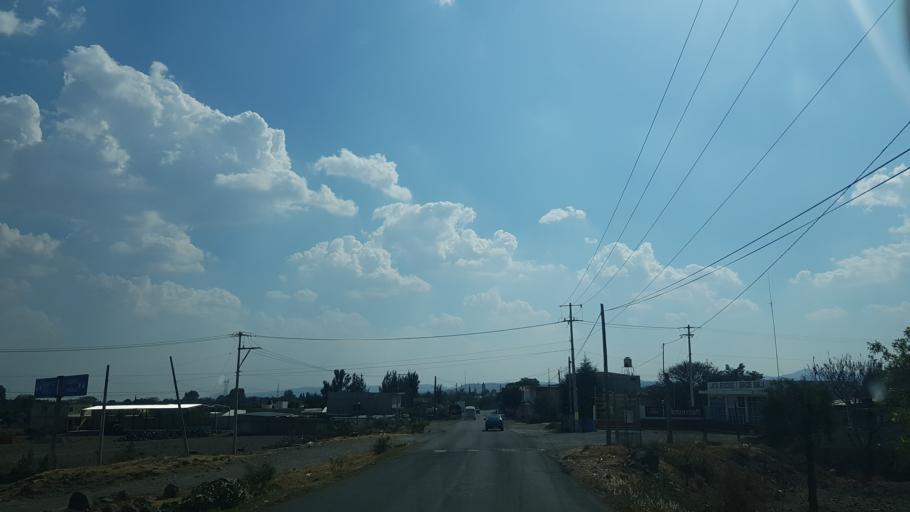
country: MX
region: Puebla
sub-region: Atlixco
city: Colonia Agricola de Ocotepec (Colonia San Jose)
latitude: 18.8945
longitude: -98.5111
